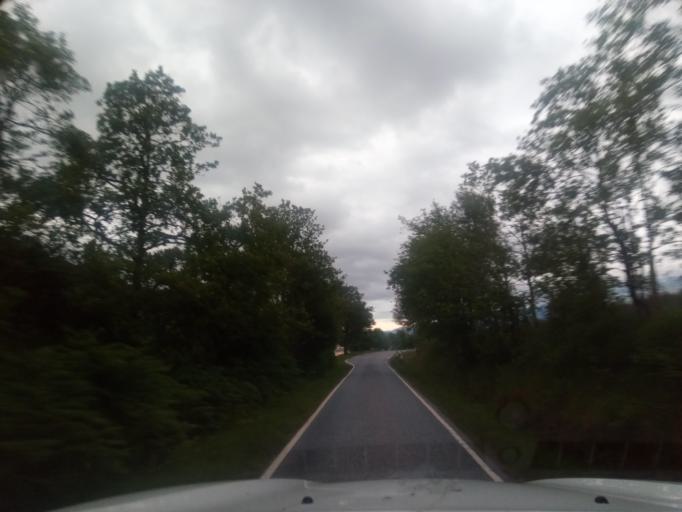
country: GB
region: Scotland
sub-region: Highland
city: Fort William
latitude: 56.8550
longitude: -5.3373
